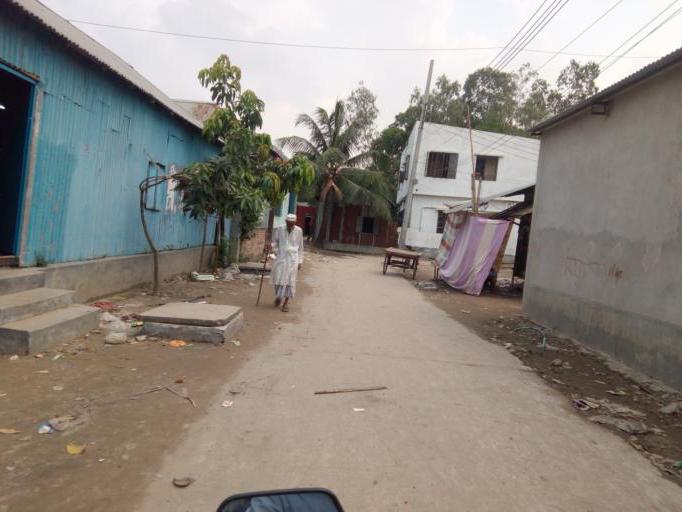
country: BD
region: Dhaka
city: Paltan
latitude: 23.7551
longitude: 90.4506
